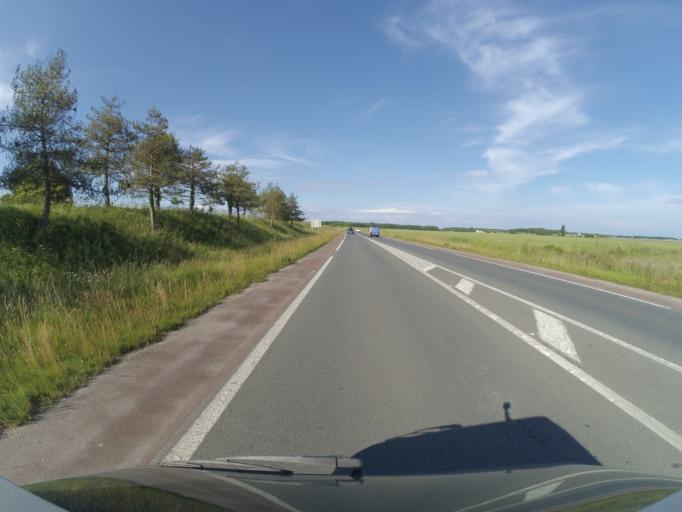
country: FR
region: Poitou-Charentes
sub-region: Departement de la Charente-Maritime
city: Saint-Sulpice-de-Royan
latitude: 45.6670
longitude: -1.0088
